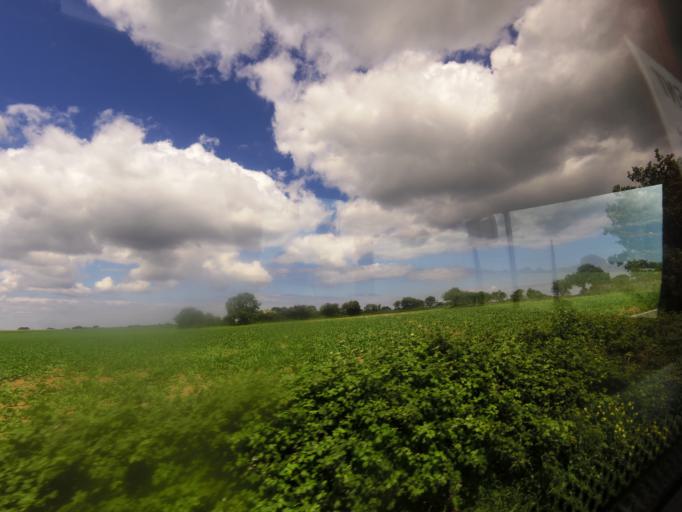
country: GB
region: England
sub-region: Norfolk
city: Cromer
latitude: 52.8765
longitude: 1.2913
